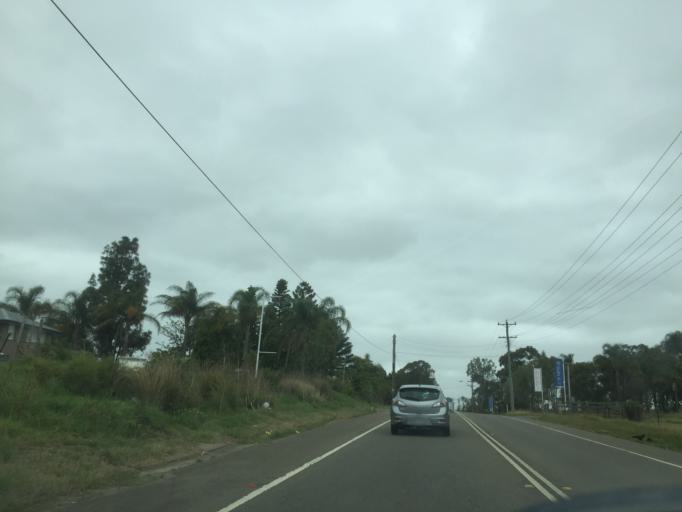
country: AU
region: New South Wales
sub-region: Blacktown
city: Stanhope Gardens
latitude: -33.7186
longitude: 150.9443
